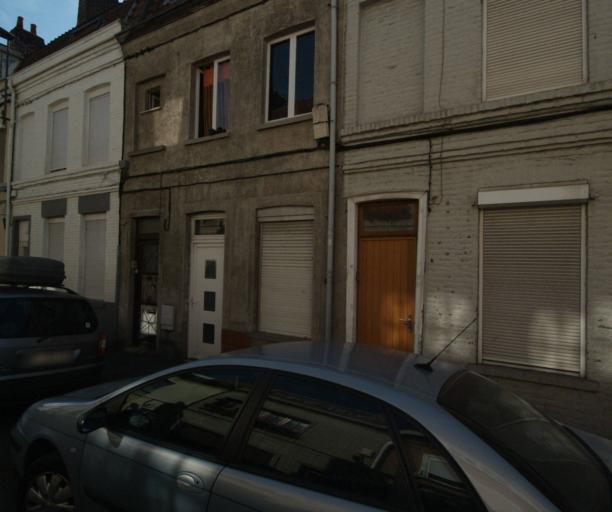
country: FR
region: Nord-Pas-de-Calais
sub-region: Departement du Nord
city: La Madeleine
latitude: 50.6334
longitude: 3.0931
